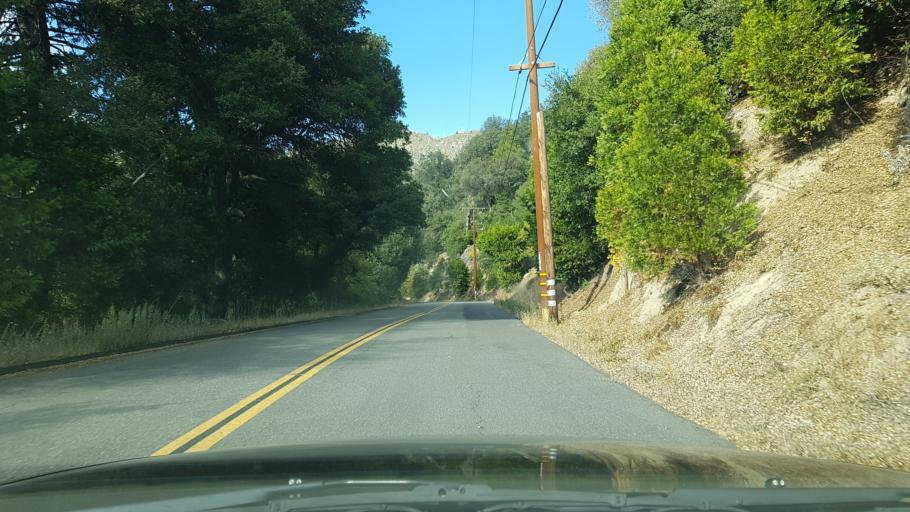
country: US
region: California
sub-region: San Diego County
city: Julian
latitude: 33.1246
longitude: -116.6015
